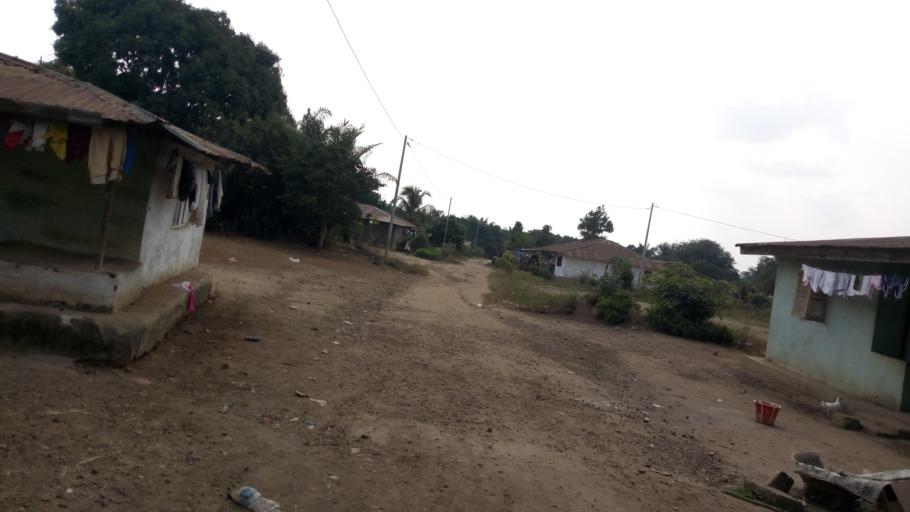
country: SL
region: Southern Province
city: Mogbwemo
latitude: 7.7630
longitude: -12.3138
